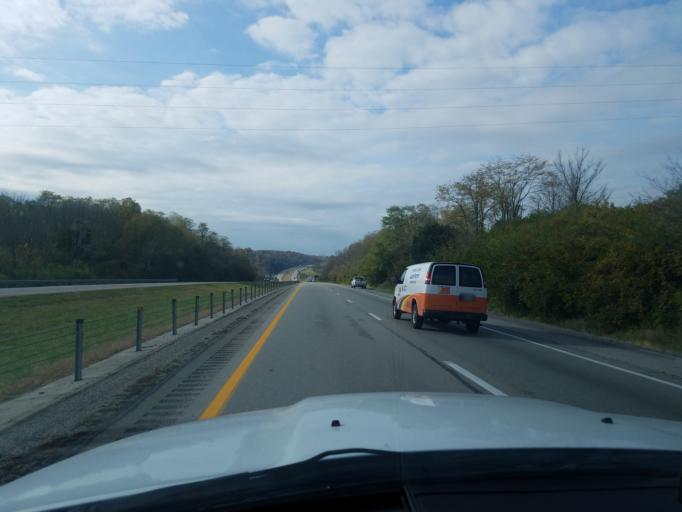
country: US
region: Kentucky
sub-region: Boone County
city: Verona
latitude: 38.8547
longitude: -84.6618
